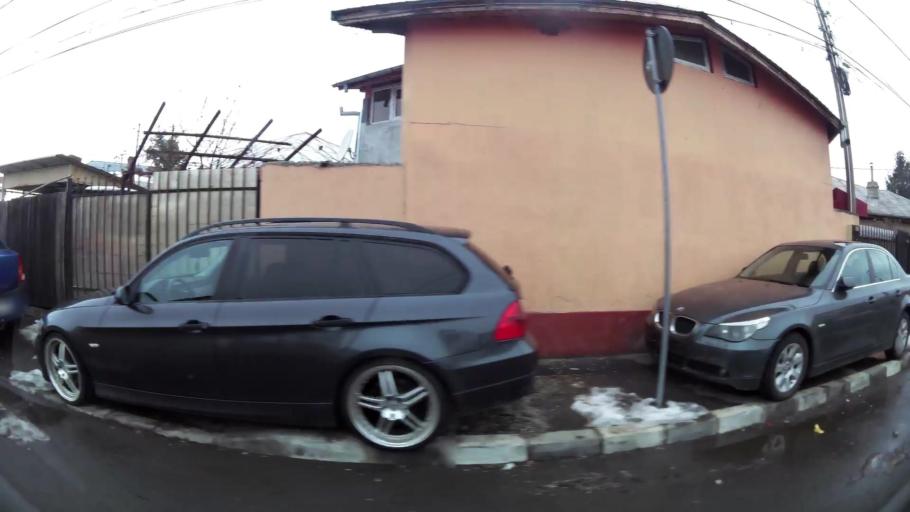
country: RO
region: Ilfov
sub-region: Comuna Pantelimon
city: Pantelimon
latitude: 44.4521
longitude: 26.2000
